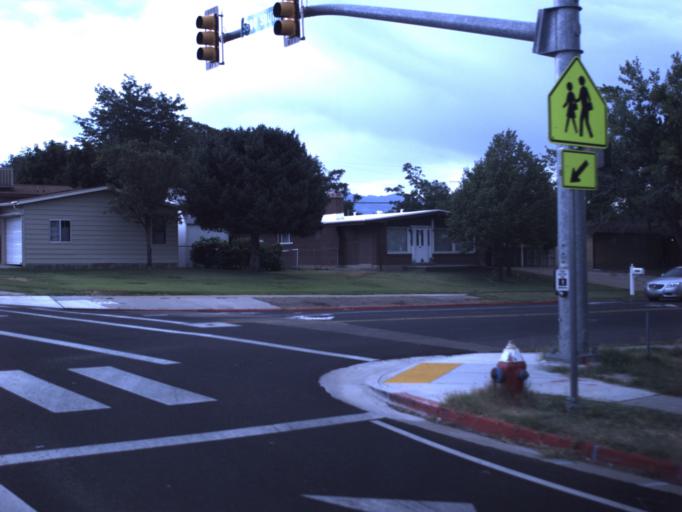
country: US
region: Utah
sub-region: Weber County
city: Roy
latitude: 41.1616
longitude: -112.0343
